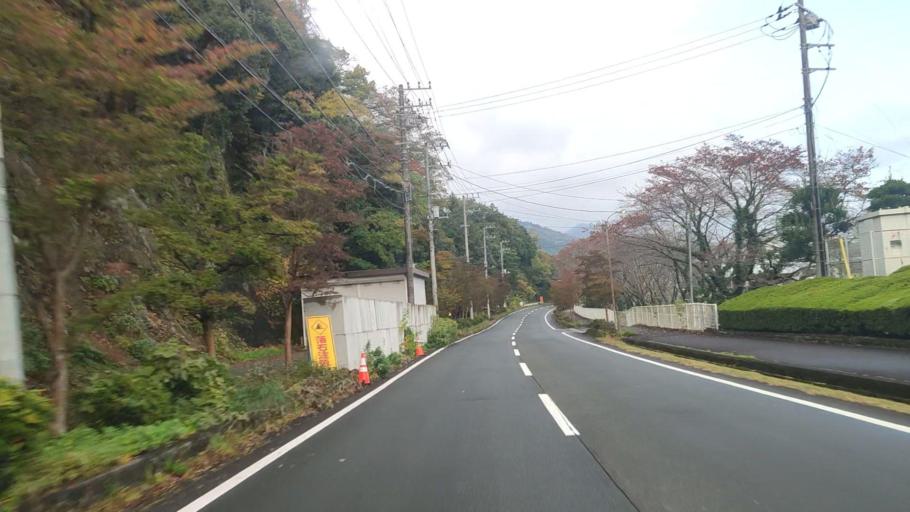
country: JP
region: Shizuoka
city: Fujinomiya
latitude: 35.2919
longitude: 138.4526
